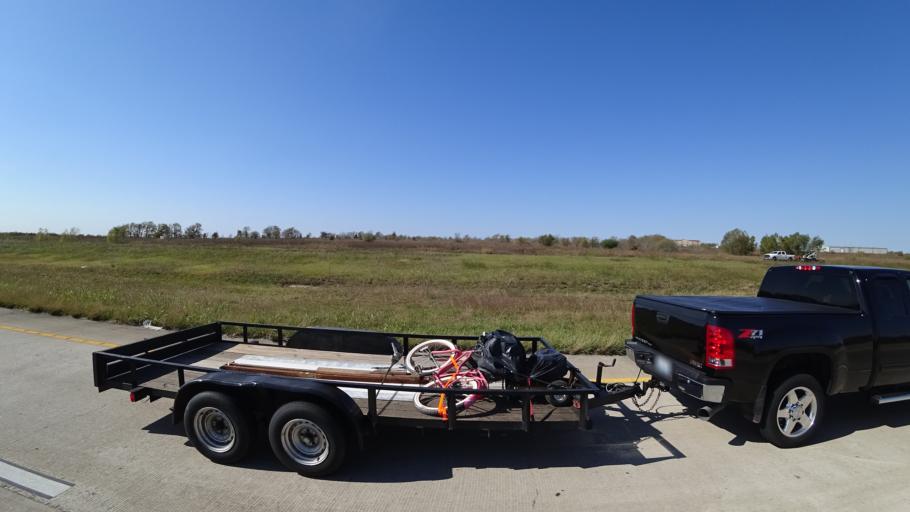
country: US
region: Texas
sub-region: Travis County
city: Manor
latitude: 30.3855
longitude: -97.5788
